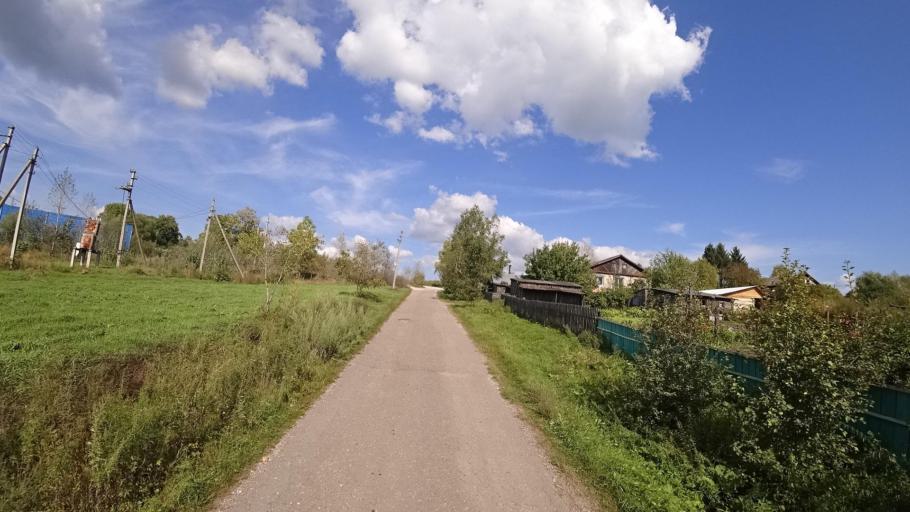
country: RU
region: Jewish Autonomous Oblast
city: Birakan
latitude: 49.0103
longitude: 131.7419
